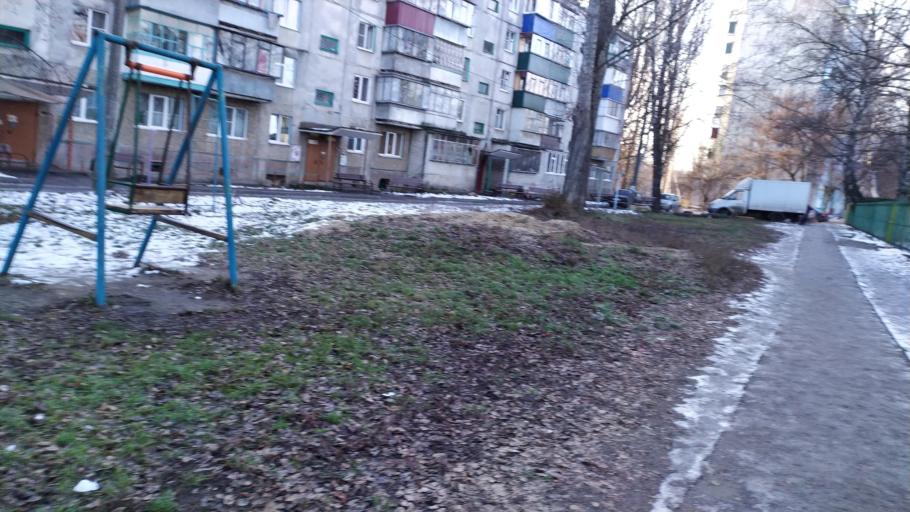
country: RU
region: Kursk
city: Kursk
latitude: 51.6501
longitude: 36.1387
